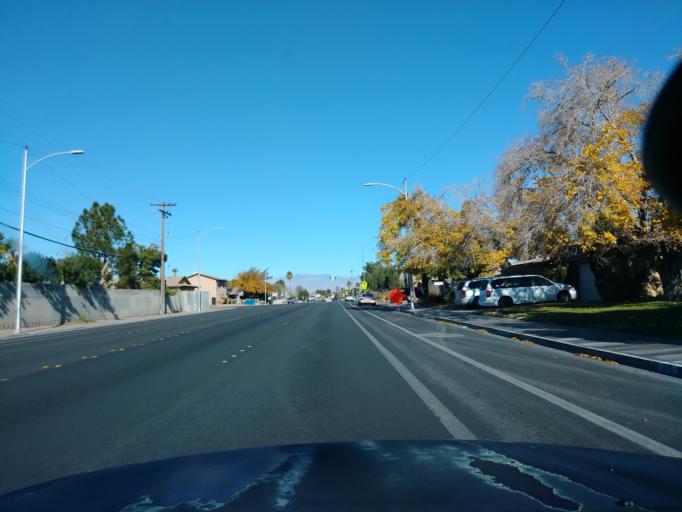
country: US
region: Nevada
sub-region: Clark County
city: Spring Valley
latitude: 36.1768
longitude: -115.2331
